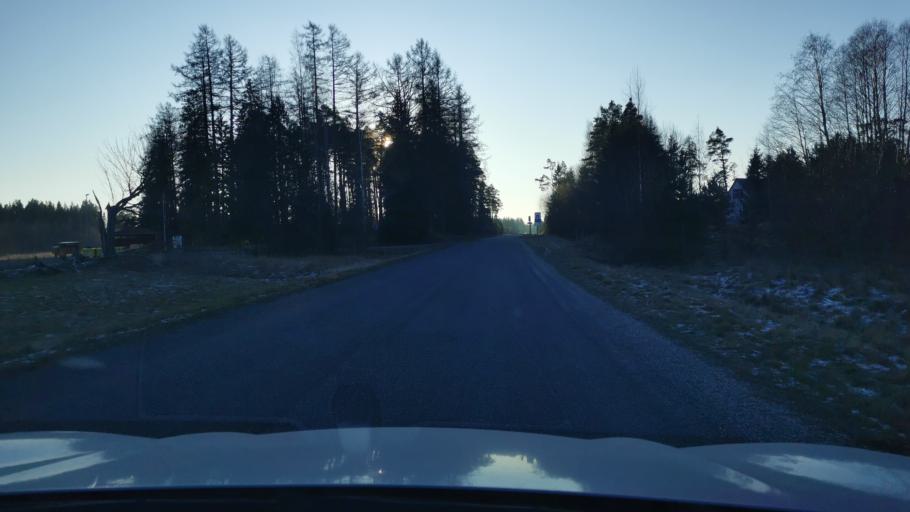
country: EE
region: Ida-Virumaa
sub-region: Kivioli linn
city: Kivioli
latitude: 59.2663
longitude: 26.9994
